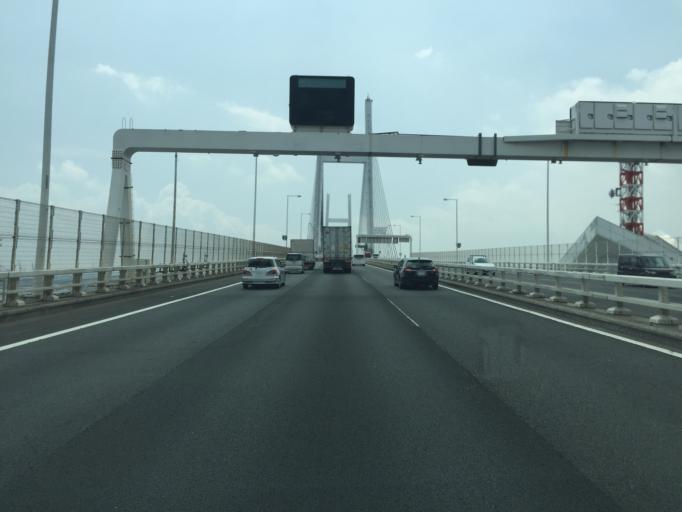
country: JP
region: Kanagawa
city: Yokohama
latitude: 35.4598
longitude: 139.6775
